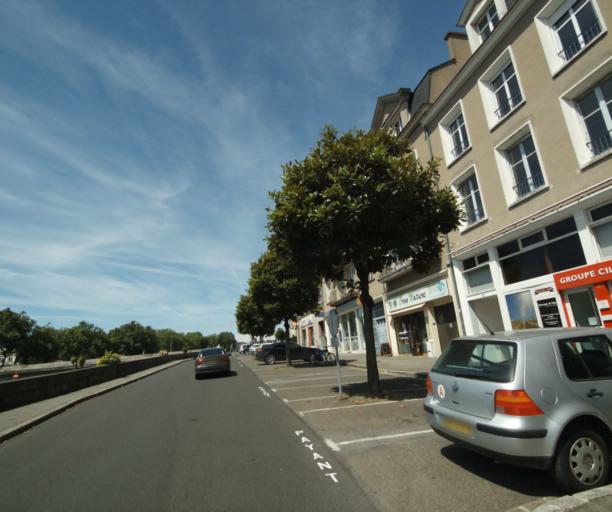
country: FR
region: Pays de la Loire
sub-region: Departement de la Mayenne
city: Laval
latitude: 48.0703
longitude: -0.7698
